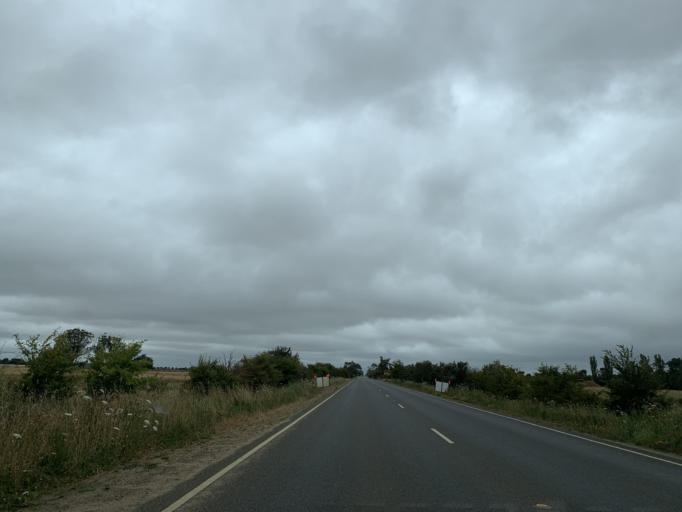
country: AU
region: Victoria
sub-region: Cardinia
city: Officer South
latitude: -38.1395
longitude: 145.3726
